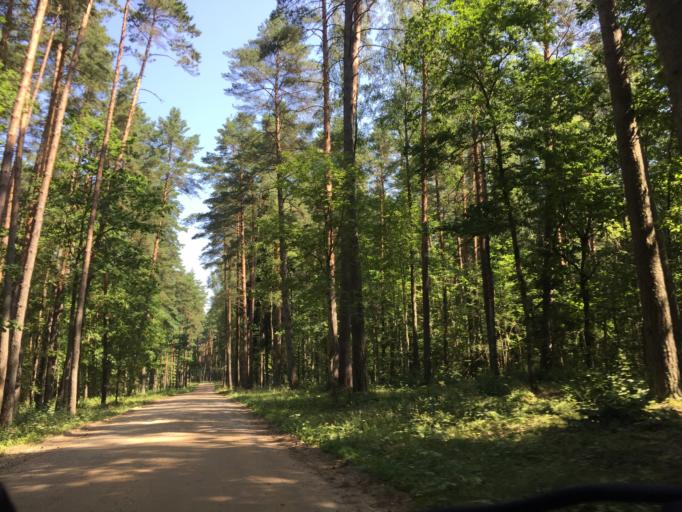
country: LV
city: Tervete
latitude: 56.4899
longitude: 23.4024
